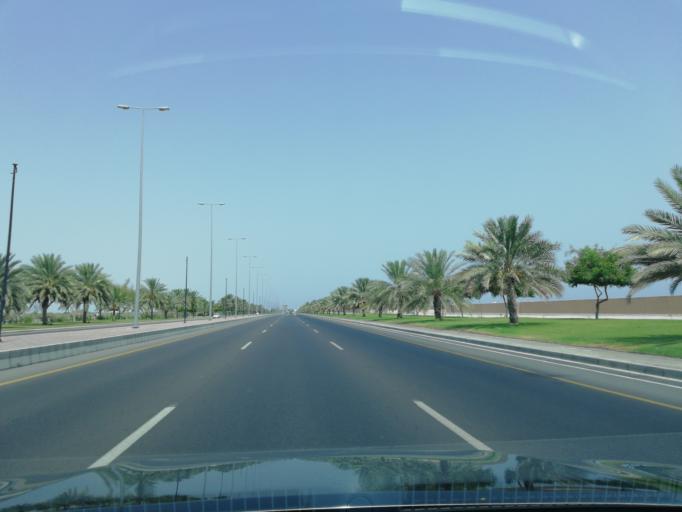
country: OM
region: Muhafazat Masqat
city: As Sib al Jadidah
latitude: 23.6873
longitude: 58.0906
